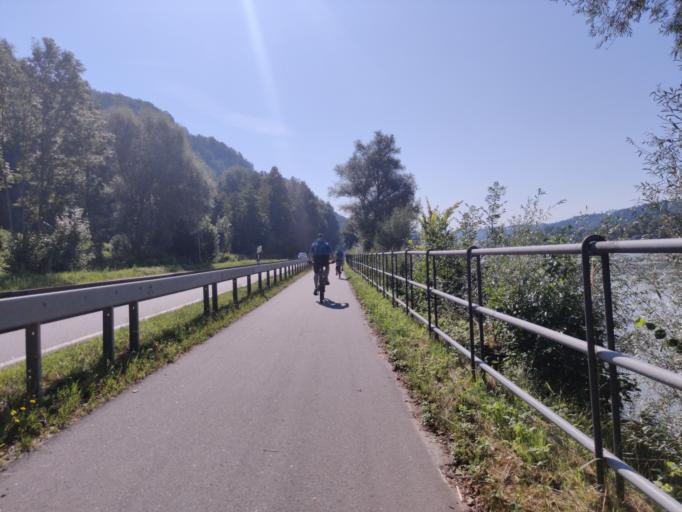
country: DE
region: Bavaria
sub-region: Lower Bavaria
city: Thyrnau
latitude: 48.5874
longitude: 13.5282
